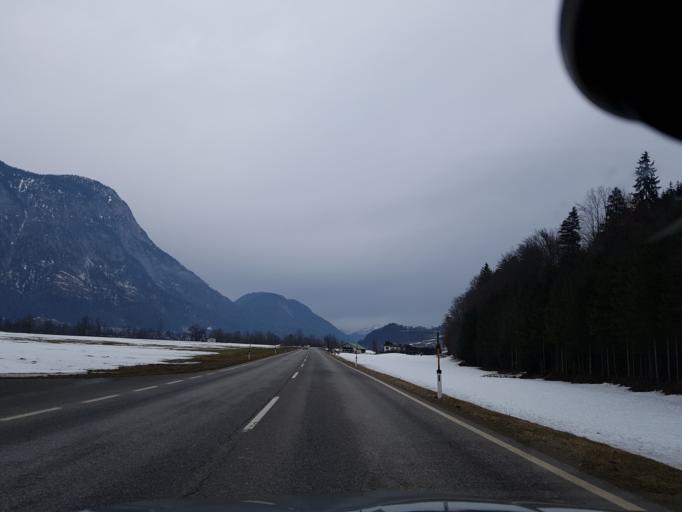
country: AT
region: Tyrol
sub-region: Politischer Bezirk Kufstein
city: Bad Haering
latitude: 47.5351
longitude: 12.1133
